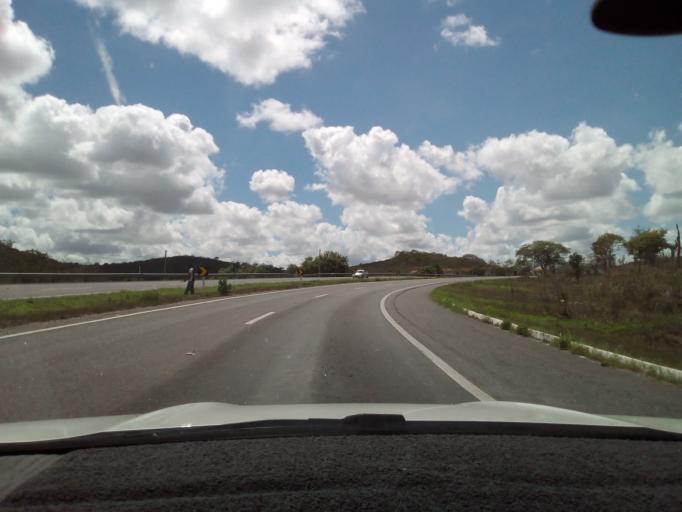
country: BR
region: Paraiba
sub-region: Massaranduba
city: Massaranduba
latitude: -7.2726
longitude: -35.7515
